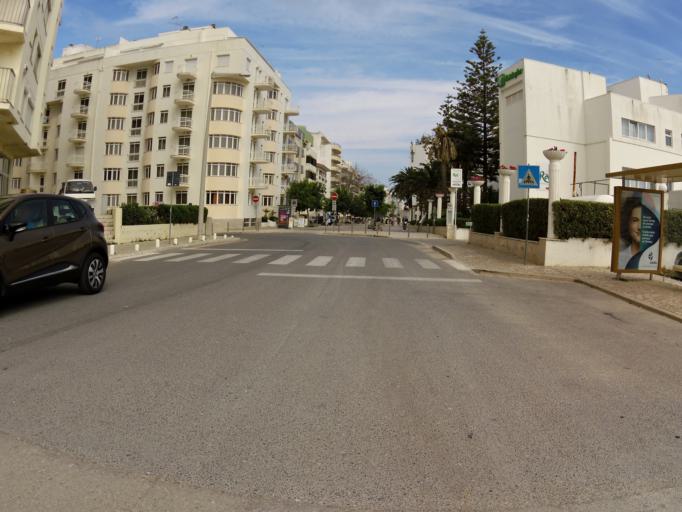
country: PT
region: Faro
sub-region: Silves
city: Armacao de Pera
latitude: 37.1028
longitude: -8.3672
